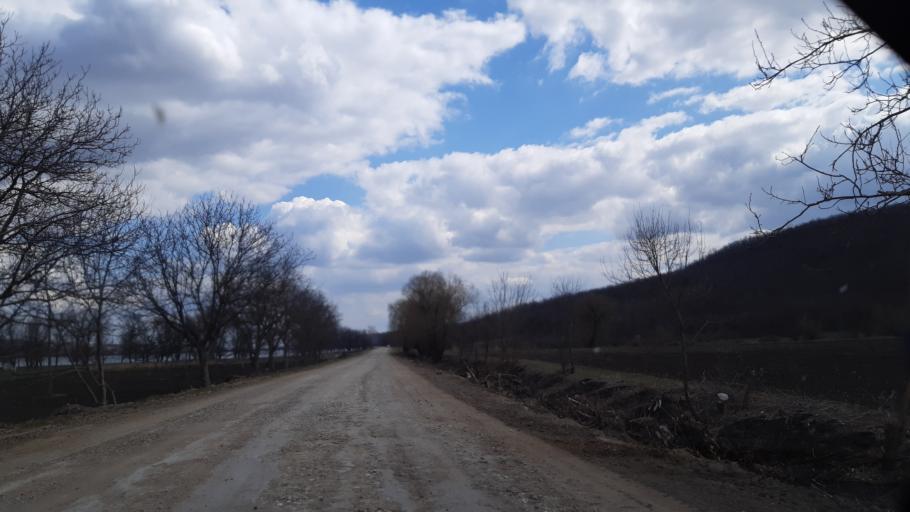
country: MD
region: Laloveni
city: Ialoveni
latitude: 46.8918
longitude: 28.7279
